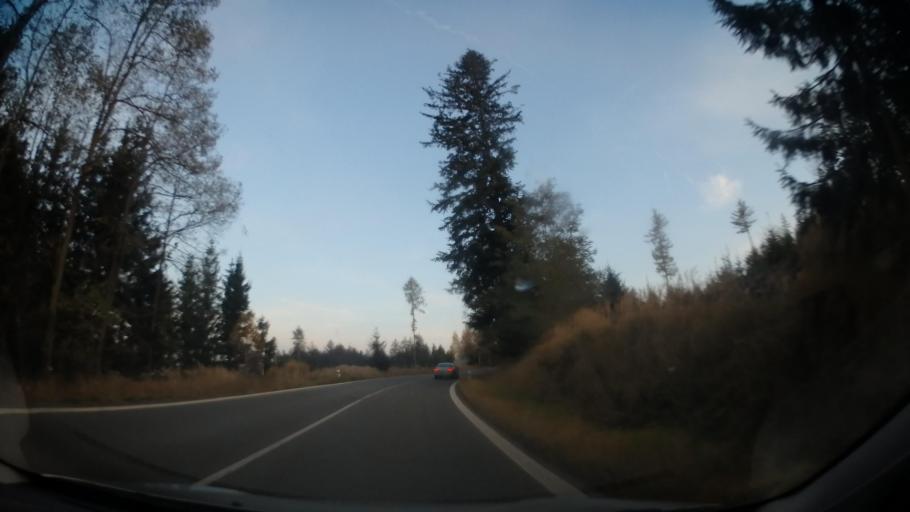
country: CZ
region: Vysocina
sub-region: Okres Pelhrimov
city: Zeliv
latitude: 49.5510
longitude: 15.1402
